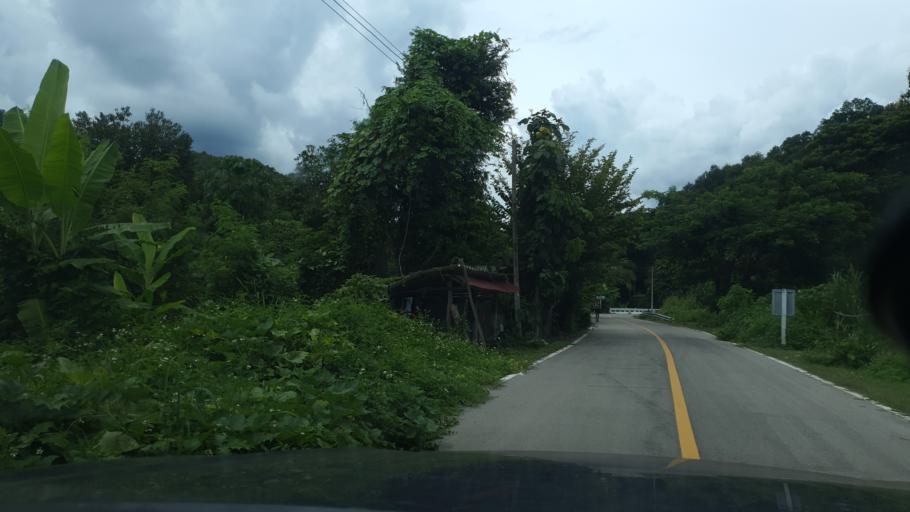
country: TH
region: Lamphun
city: Mae Tha
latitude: 18.4362
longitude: 99.2682
